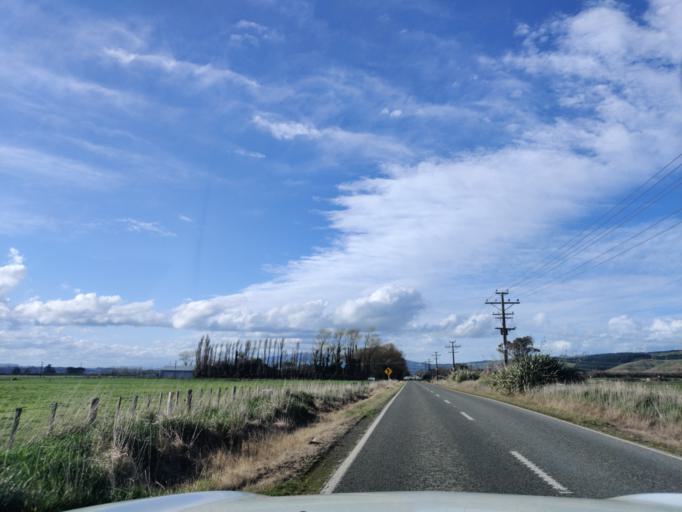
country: NZ
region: Manawatu-Wanganui
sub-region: Palmerston North City
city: Palmerston North
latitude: -40.3499
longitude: 175.6996
